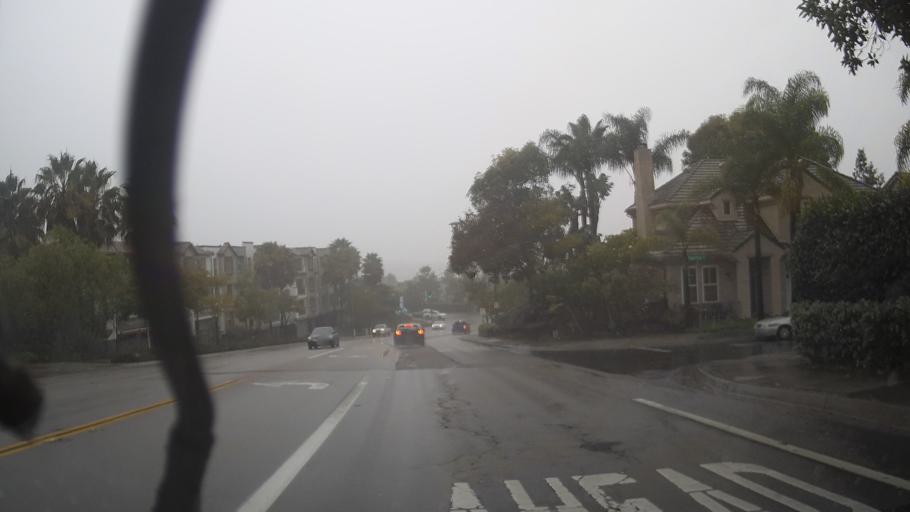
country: US
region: California
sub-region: San Diego County
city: Encinitas
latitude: 33.0591
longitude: -117.2673
